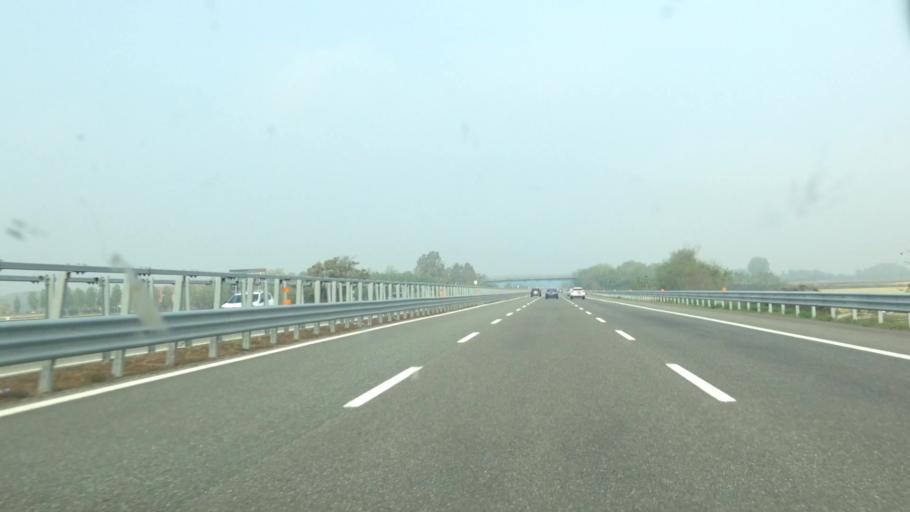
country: IT
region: Piedmont
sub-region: Provincia di Alessandria
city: Borgo San Martino
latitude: 45.0883
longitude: 8.5032
